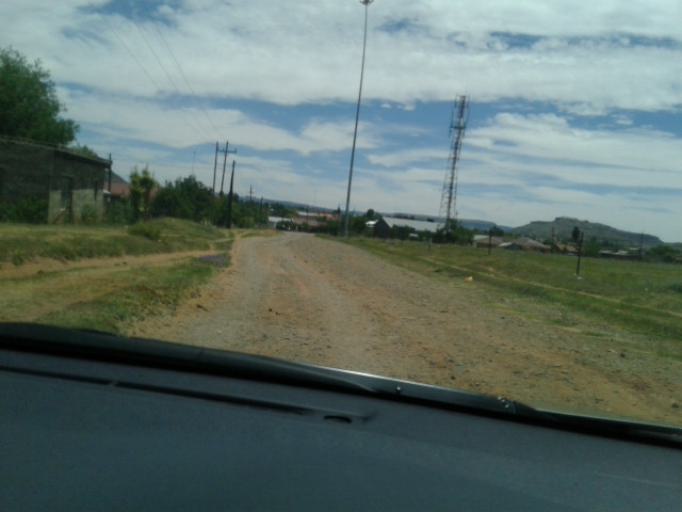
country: LS
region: Maseru
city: Maseru
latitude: -29.2941
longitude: 27.5359
